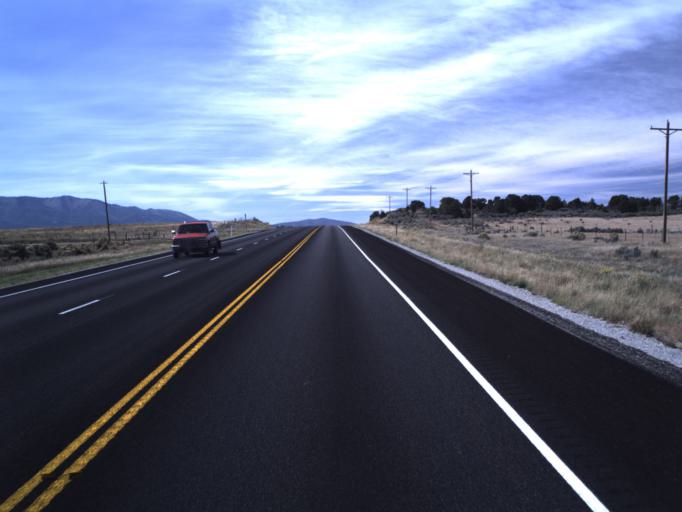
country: US
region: Utah
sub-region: San Juan County
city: Monticello
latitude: 37.8642
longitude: -109.2255
